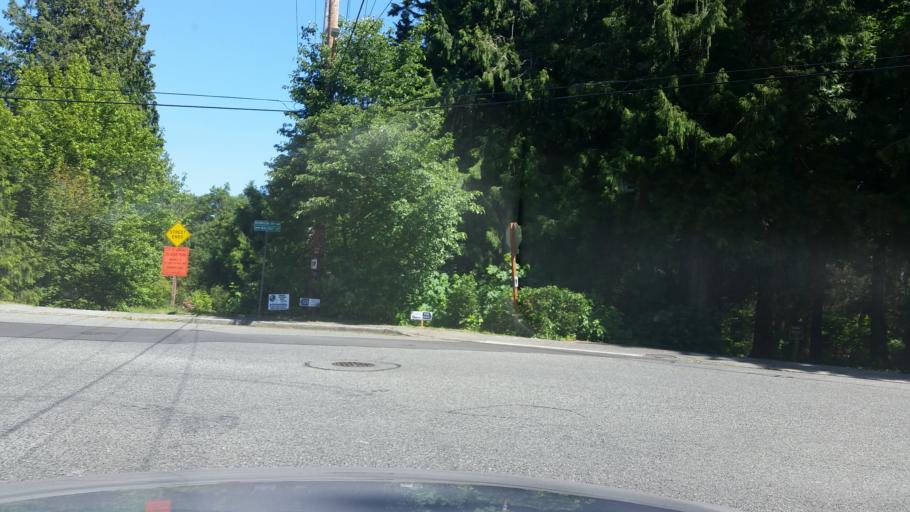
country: US
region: Washington
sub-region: Snohomish County
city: Edmonds
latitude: 47.8071
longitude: -122.3615
